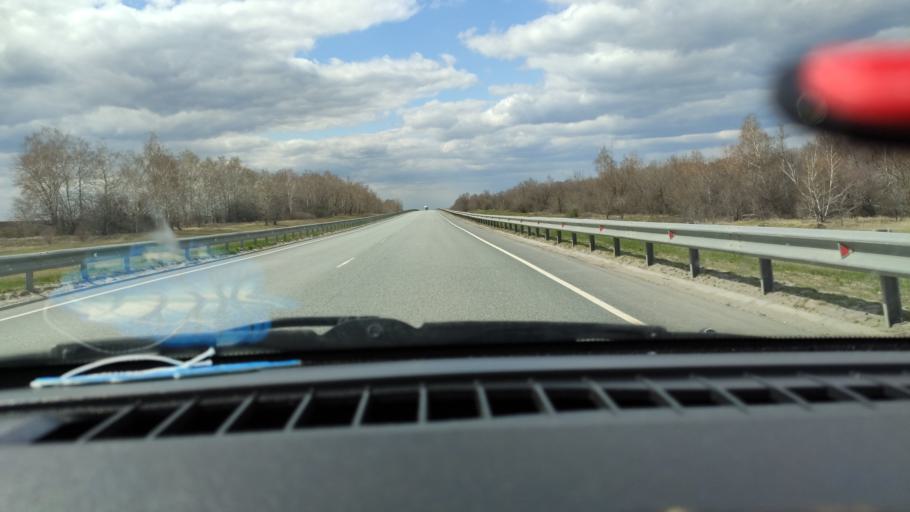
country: RU
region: Saratov
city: Balakovo
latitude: 52.0881
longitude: 47.6871
